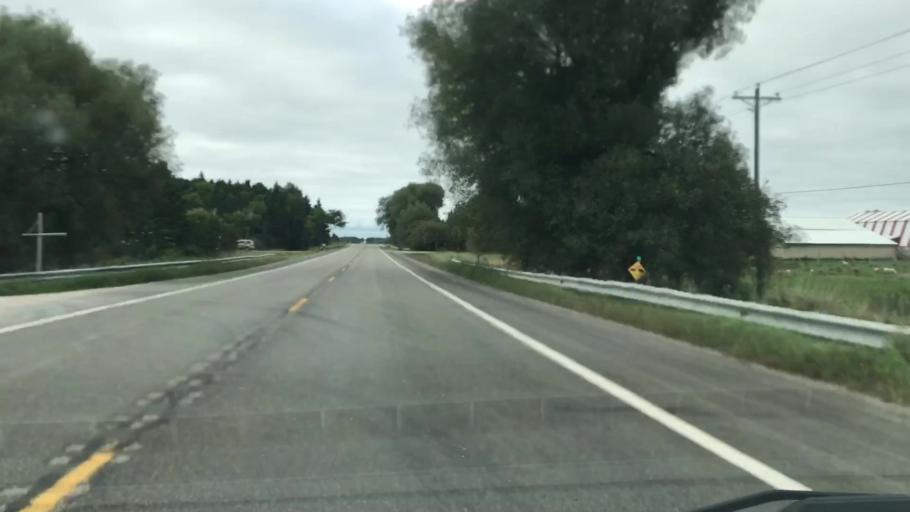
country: US
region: Michigan
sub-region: Luce County
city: Newberry
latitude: 46.1572
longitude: -85.5713
